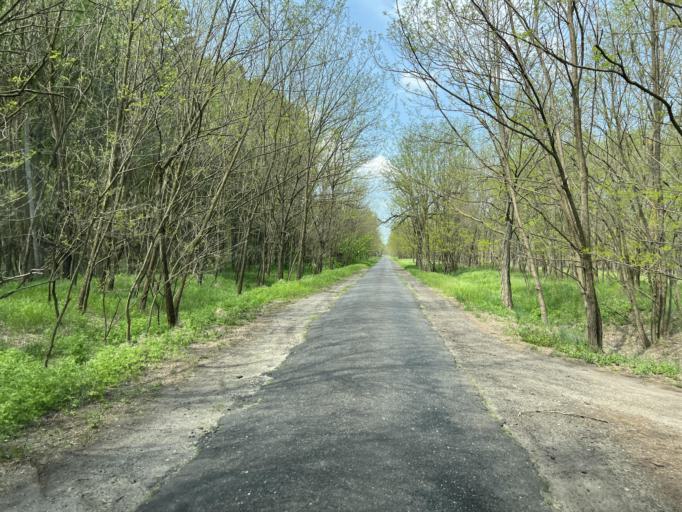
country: HU
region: Pest
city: Kocser
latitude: 47.0502
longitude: 19.9019
